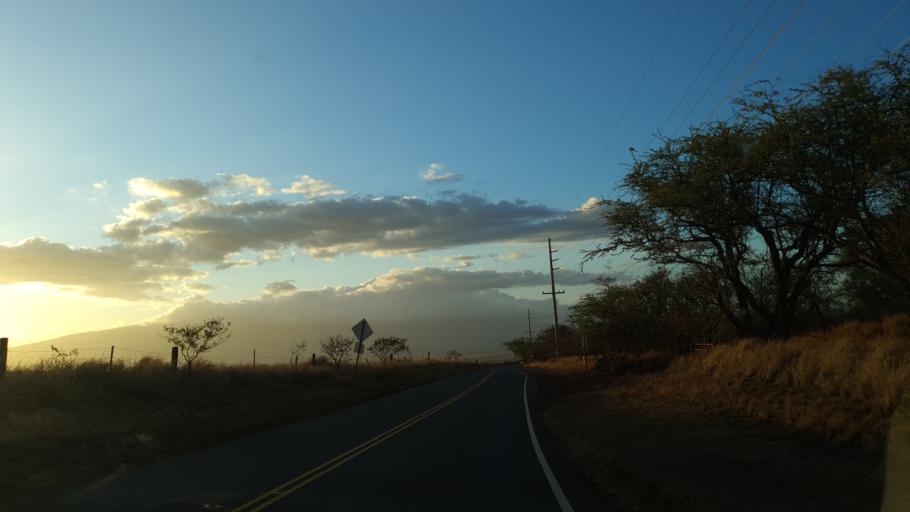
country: US
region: Hawaii
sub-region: Maui County
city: Pukalani
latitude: 20.7961
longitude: -156.3695
